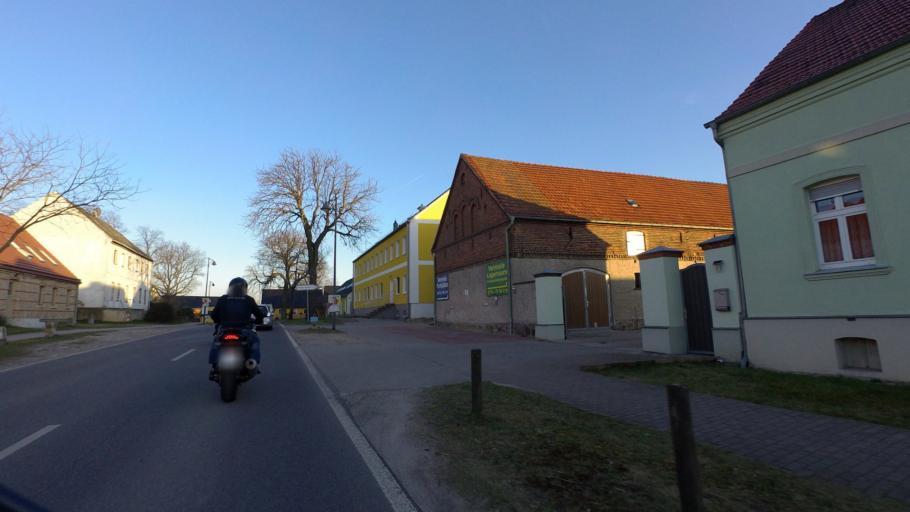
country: DE
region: Berlin
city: Hellersdorf
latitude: 52.5691
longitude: 13.6188
